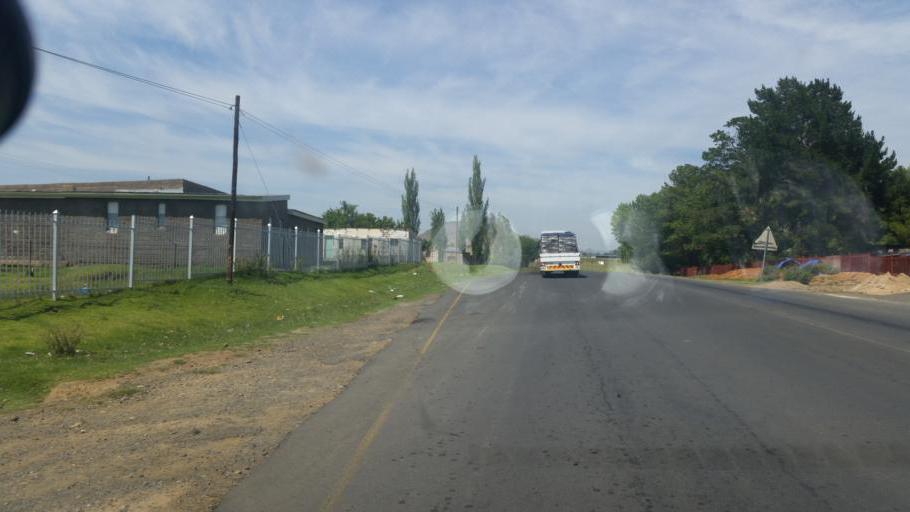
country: LS
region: Mafeteng
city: Mafeteng
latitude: -29.7063
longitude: 27.4271
